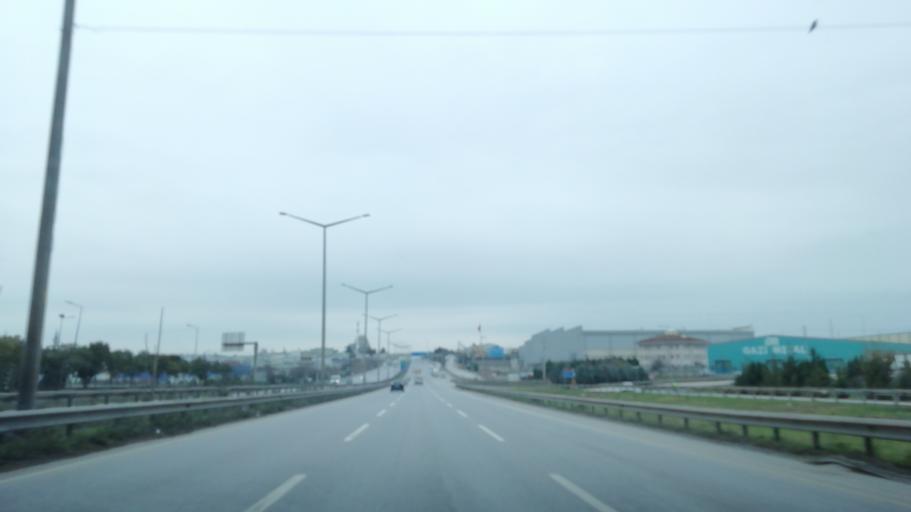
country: TR
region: Kocaeli
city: Gebze
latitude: 40.8003
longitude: 29.4606
